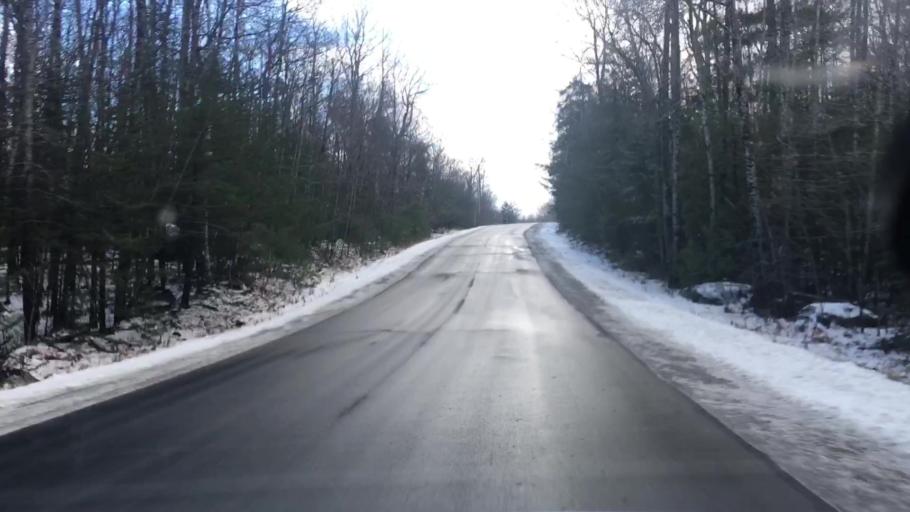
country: US
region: Maine
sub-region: Hancock County
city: Dedham
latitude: 44.6873
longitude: -68.7134
